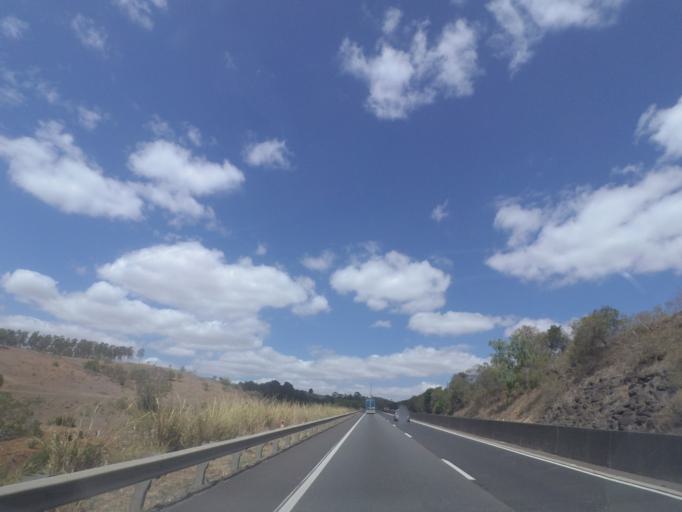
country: AU
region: Queensland
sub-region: Ipswich
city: Thagoona
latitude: -27.5643
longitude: 152.5732
